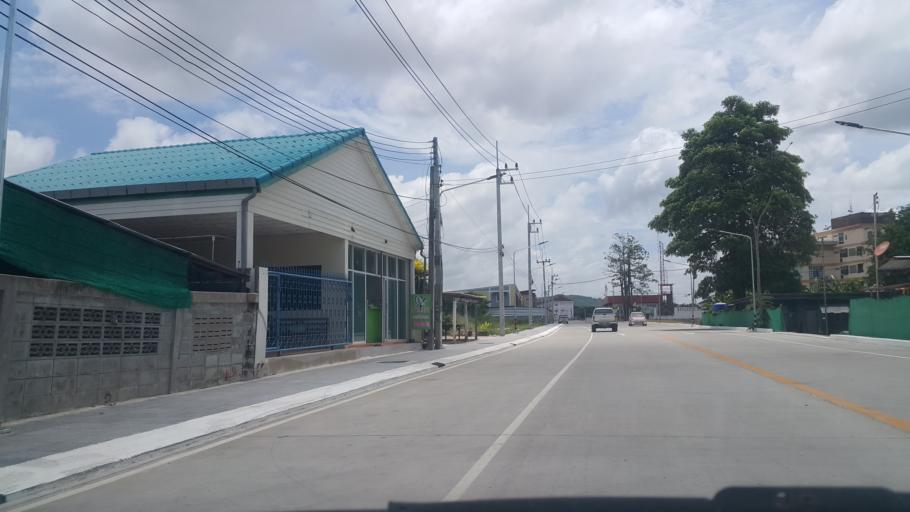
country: TH
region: Rayong
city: Ban Chang
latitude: 12.7190
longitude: 101.0666
